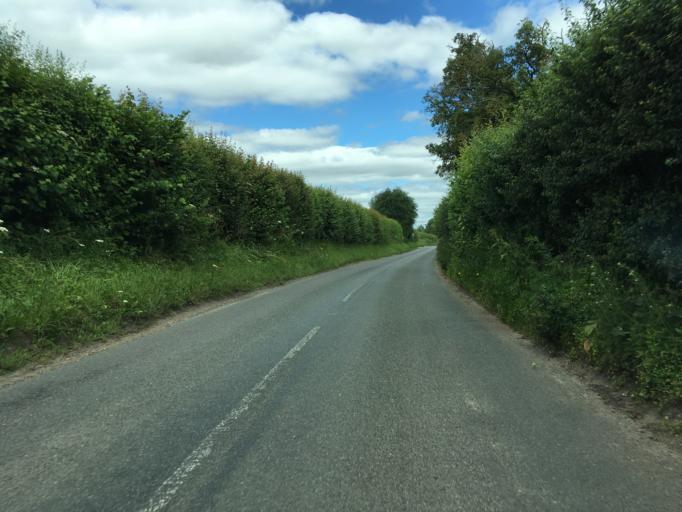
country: GB
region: England
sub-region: West Berkshire
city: Welford
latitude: 51.4310
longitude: -1.3827
